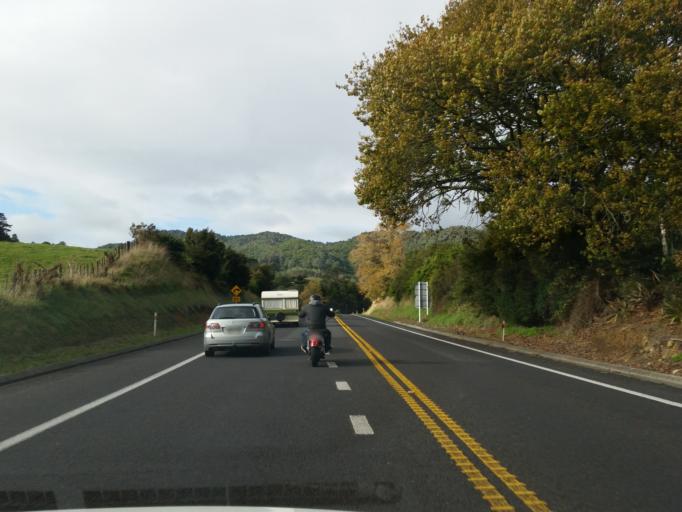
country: NZ
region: Waikato
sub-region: Hauraki District
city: Paeroa
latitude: -37.4027
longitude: 175.7014
